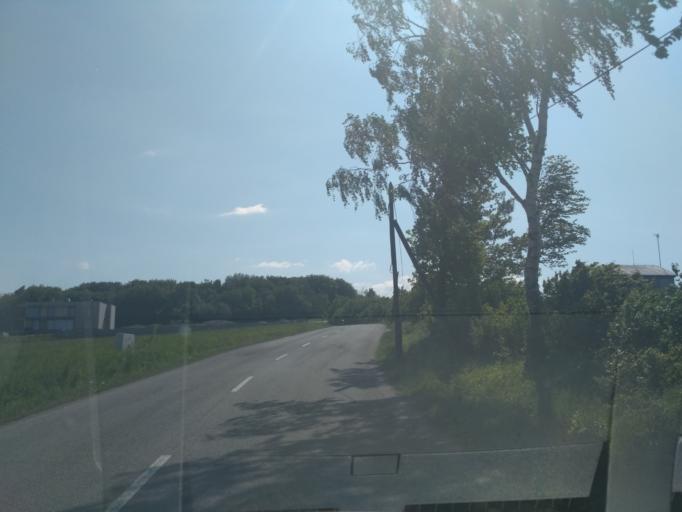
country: SK
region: Presovsky
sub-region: Okres Presov
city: Presov
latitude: 48.9463
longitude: 21.2955
